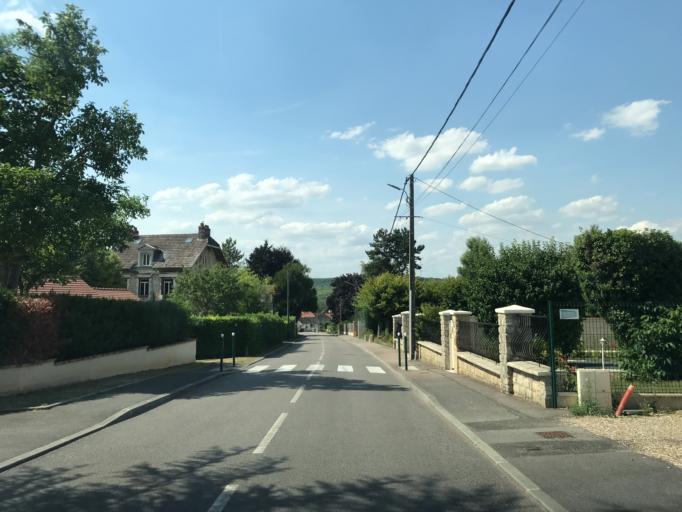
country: FR
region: Haute-Normandie
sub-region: Departement de l'Eure
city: Gasny
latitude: 49.0736
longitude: 1.5962
